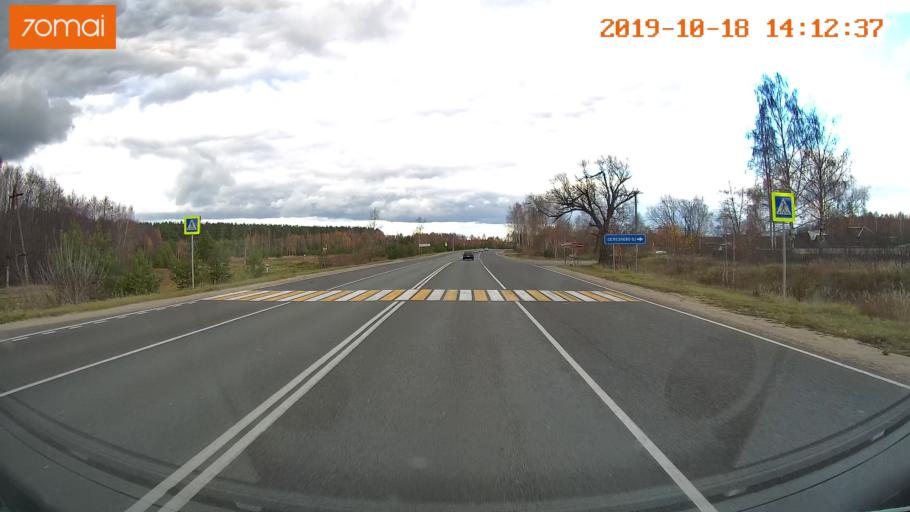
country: RU
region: Rjazan
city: Spas-Klepiki
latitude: 55.1472
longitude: 40.2541
